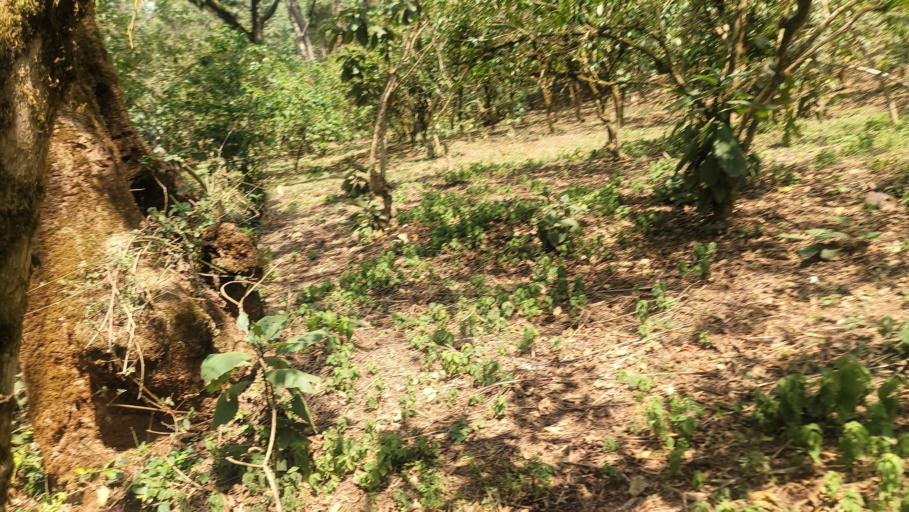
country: ET
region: Oromiya
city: Agaro
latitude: 7.7965
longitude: 36.4885
